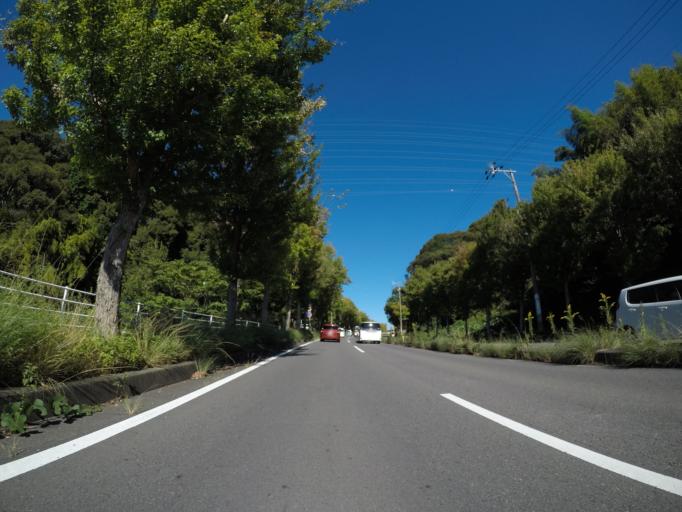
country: JP
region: Shizuoka
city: Fujieda
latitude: 34.8576
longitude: 138.2412
